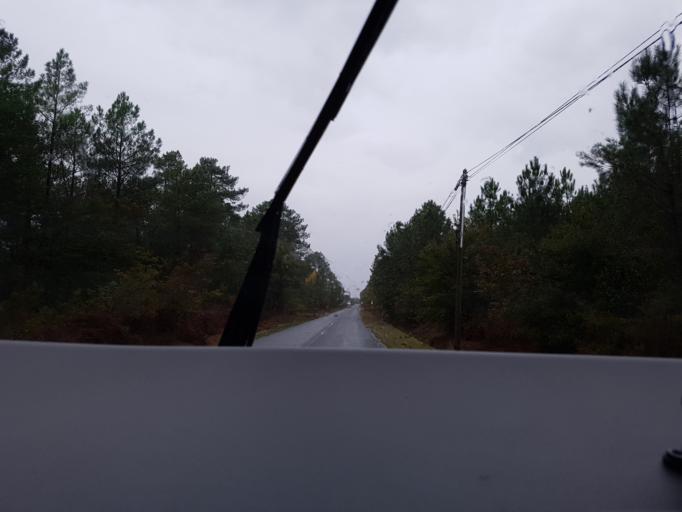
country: FR
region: Aquitaine
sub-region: Departement de la Gironde
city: Saint-Symphorien
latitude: 44.3490
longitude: -0.6178
